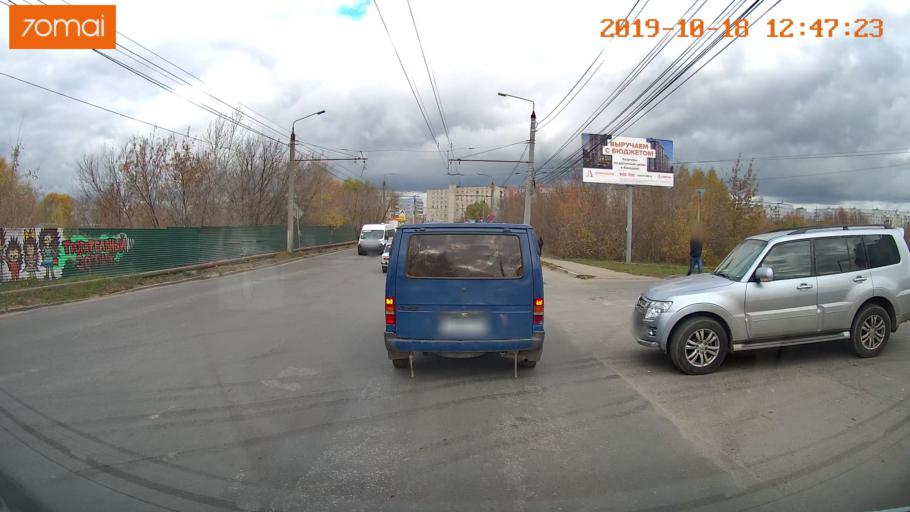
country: RU
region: Rjazan
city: Ryazan'
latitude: 54.6581
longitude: 39.6632
